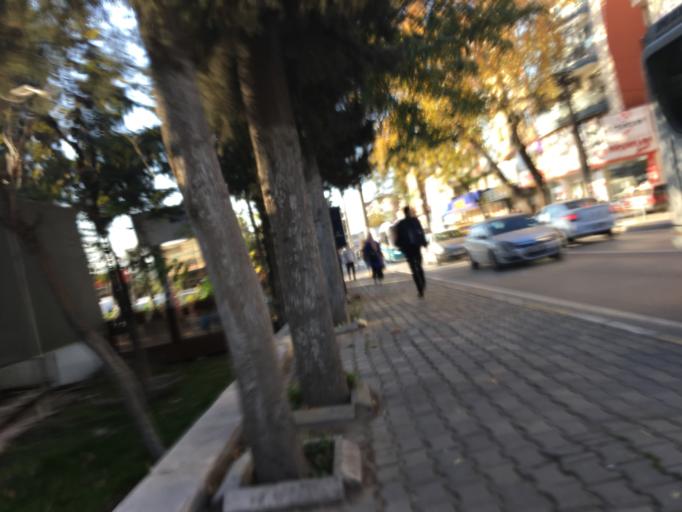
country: TR
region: Izmir
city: Buca
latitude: 38.3826
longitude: 27.1742
